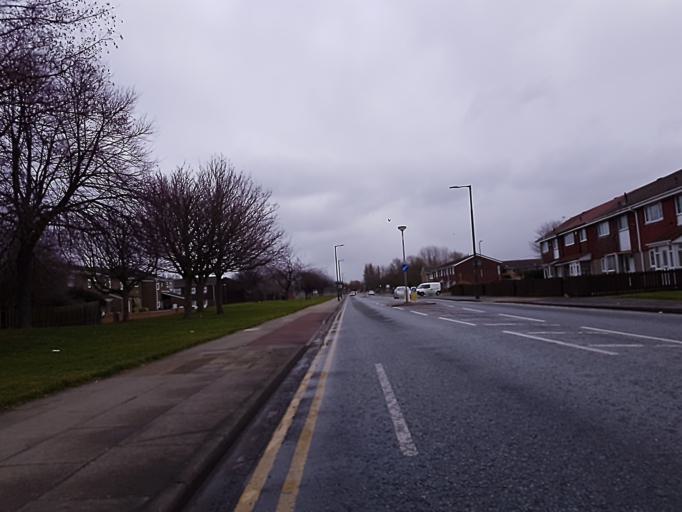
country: GB
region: England
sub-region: North East Lincolnshire
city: Great Coates
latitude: 53.5709
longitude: -0.1216
